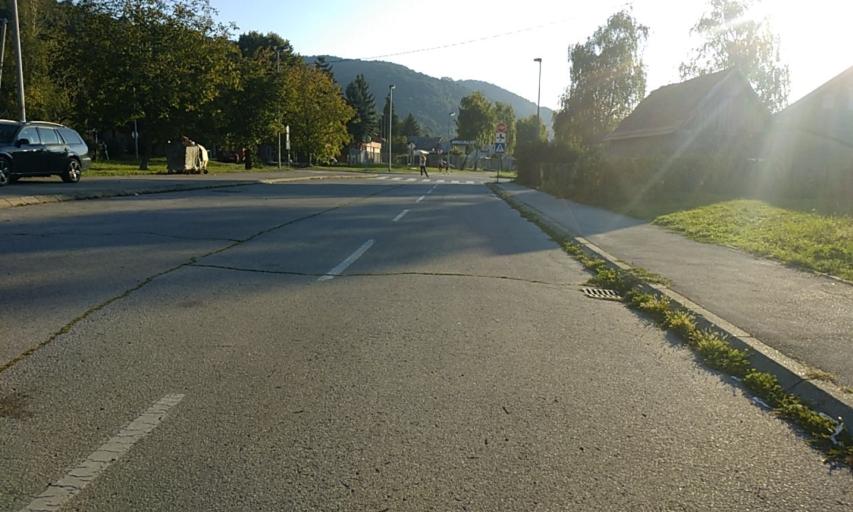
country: BA
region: Republika Srpska
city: Hiseti
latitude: 44.7563
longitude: 17.1825
